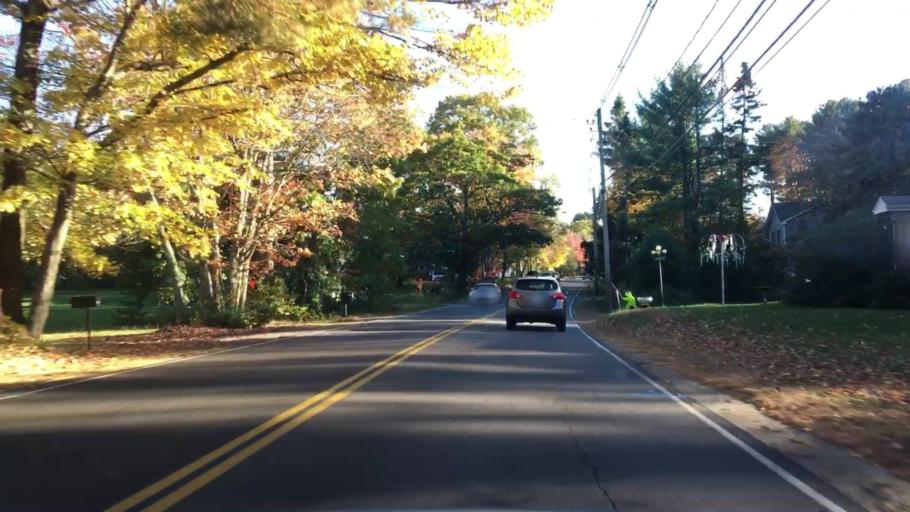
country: US
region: Maine
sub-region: Cumberland County
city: Scarborough
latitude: 43.6095
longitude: -70.3396
